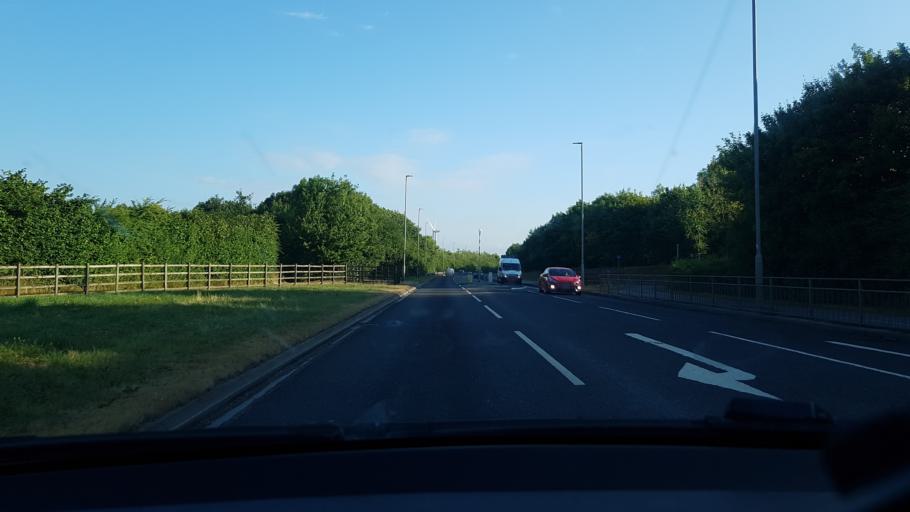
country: GB
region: England
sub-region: Nottinghamshire
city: Awsworth
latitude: 52.9858
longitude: -1.2916
